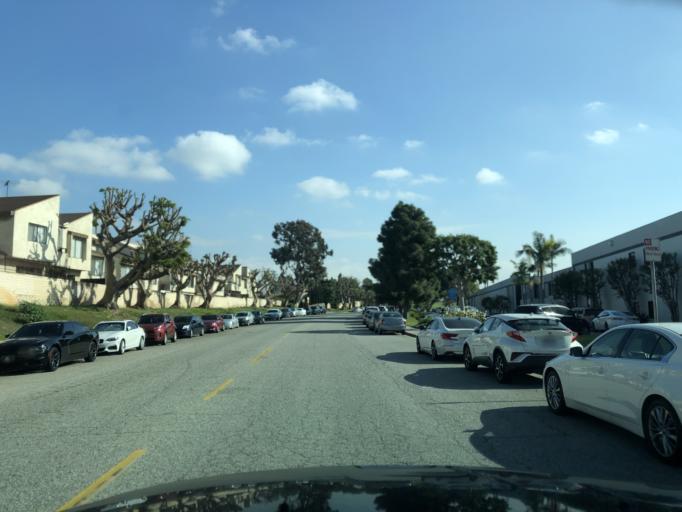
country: US
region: California
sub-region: Los Angeles County
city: Inglewood
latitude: 33.9685
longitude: -118.3648
